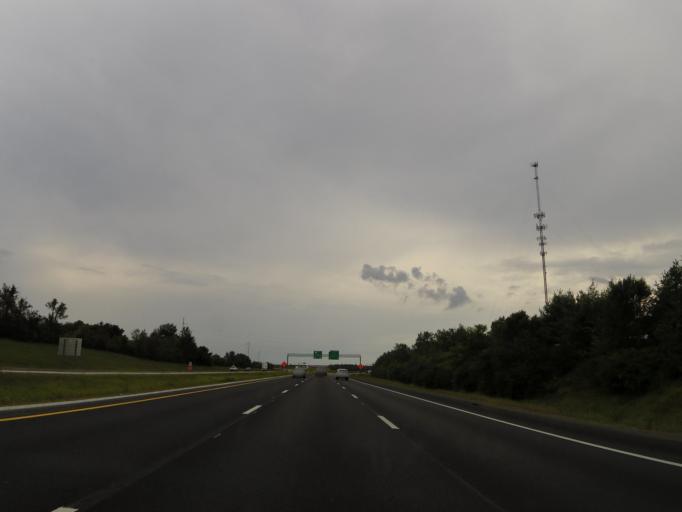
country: US
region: Tennessee
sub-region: Rutherford County
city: Murfreesboro
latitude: 35.8925
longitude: -86.4692
